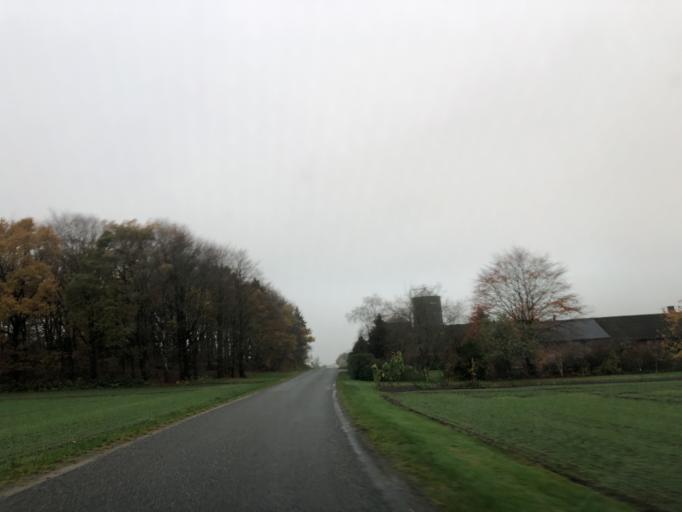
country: DK
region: Central Jutland
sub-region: Herning Kommune
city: Vildbjerg
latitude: 56.2023
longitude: 8.6888
